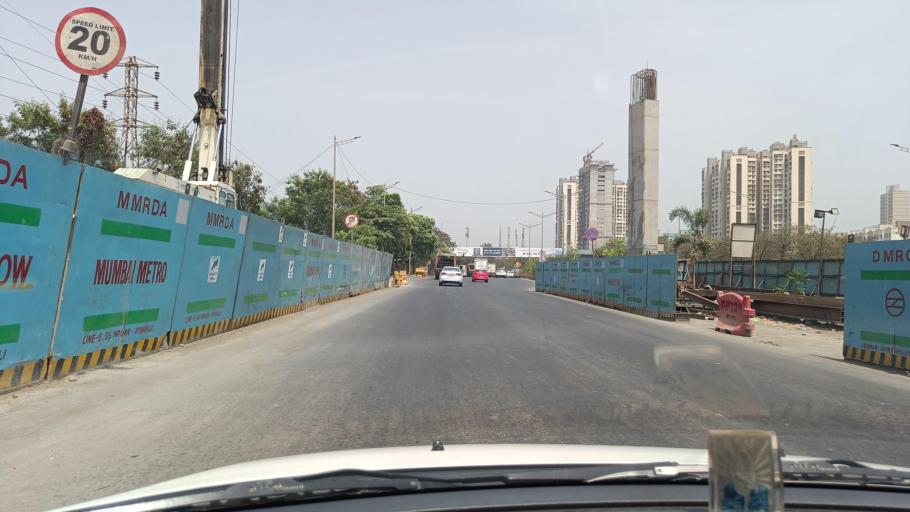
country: IN
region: Maharashtra
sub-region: Mumbai Suburban
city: Powai
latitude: 19.1250
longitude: 72.9364
